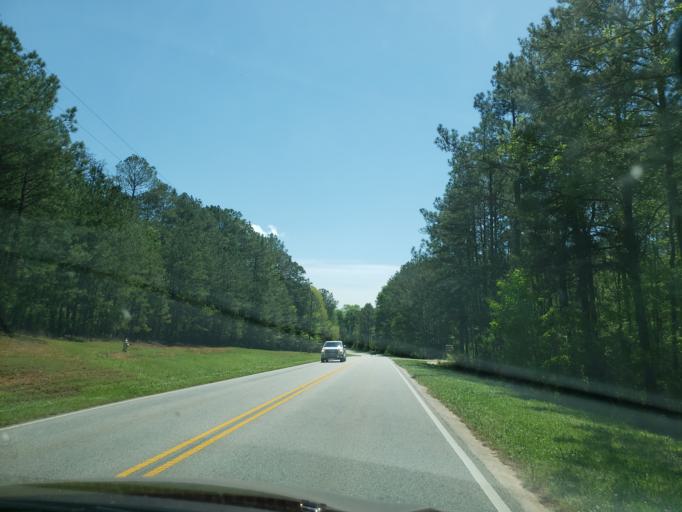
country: US
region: Alabama
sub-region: Lee County
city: Auburn
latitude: 32.6475
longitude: -85.5124
